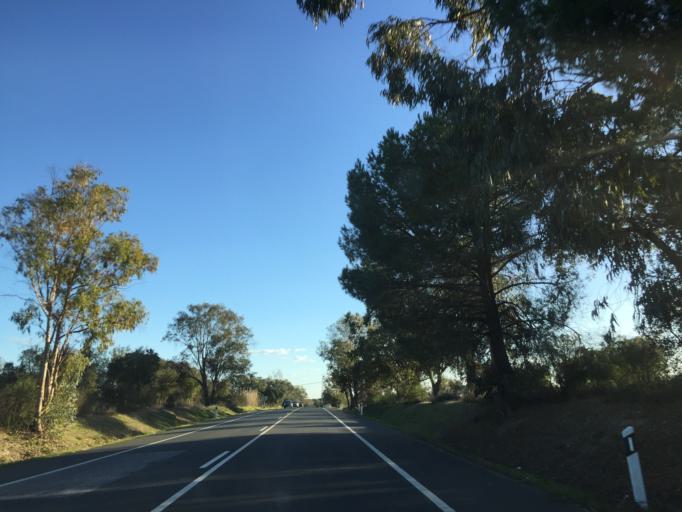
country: PT
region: Setubal
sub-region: Grandola
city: Grandola
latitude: 38.0266
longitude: -8.3997
